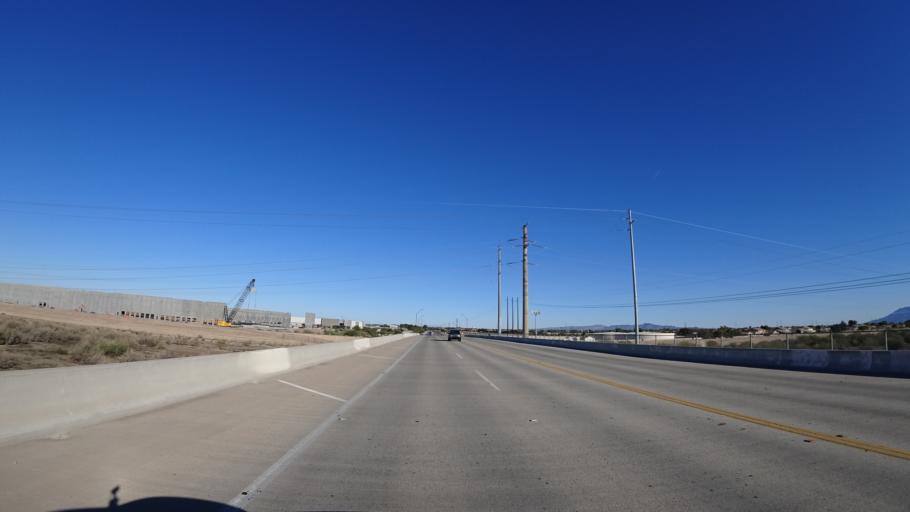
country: US
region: Arizona
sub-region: Maricopa County
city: Avondale
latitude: 33.4497
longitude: -112.3328
